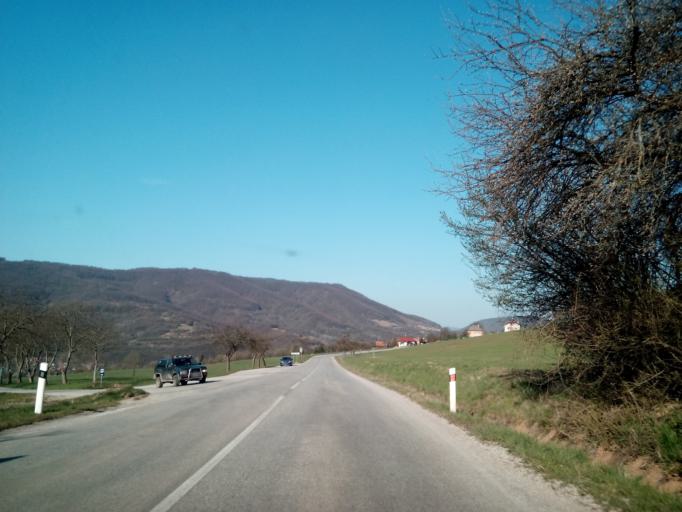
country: SK
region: Kosicky
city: Roznava
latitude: 48.6600
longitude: 20.4723
